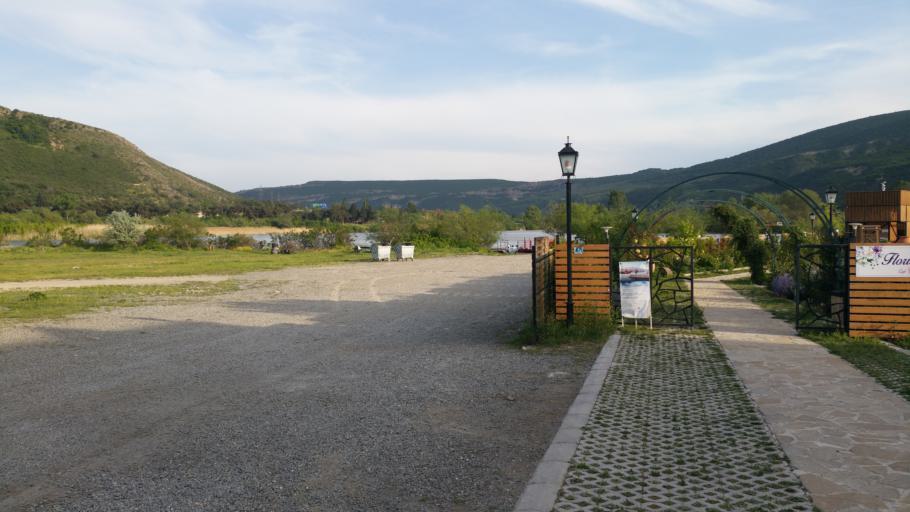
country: GE
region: Mtskheta-Mtianeti
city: Mtskheta
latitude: 41.8411
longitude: 44.7240
